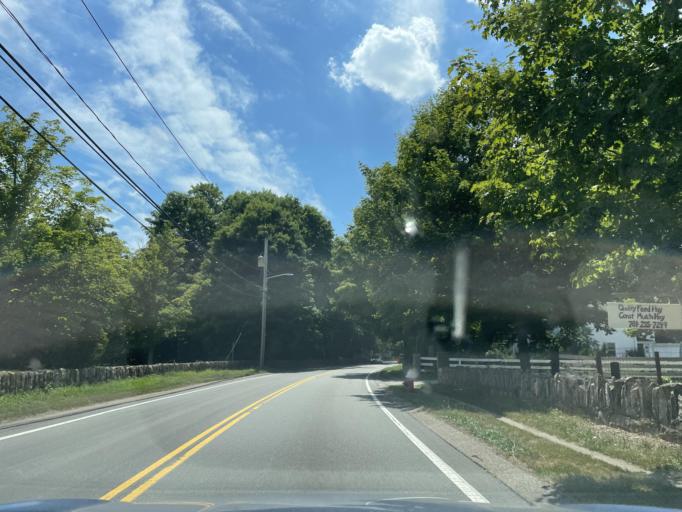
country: US
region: Massachusetts
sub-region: Norfolk County
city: Wellesley
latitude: 42.2776
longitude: -71.3098
